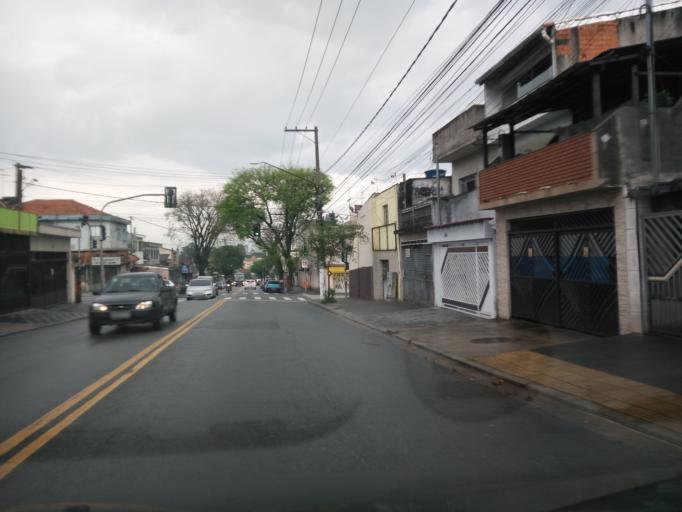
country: BR
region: Sao Paulo
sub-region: Sao Bernardo Do Campo
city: Sao Bernardo do Campo
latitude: -23.7212
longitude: -46.5844
